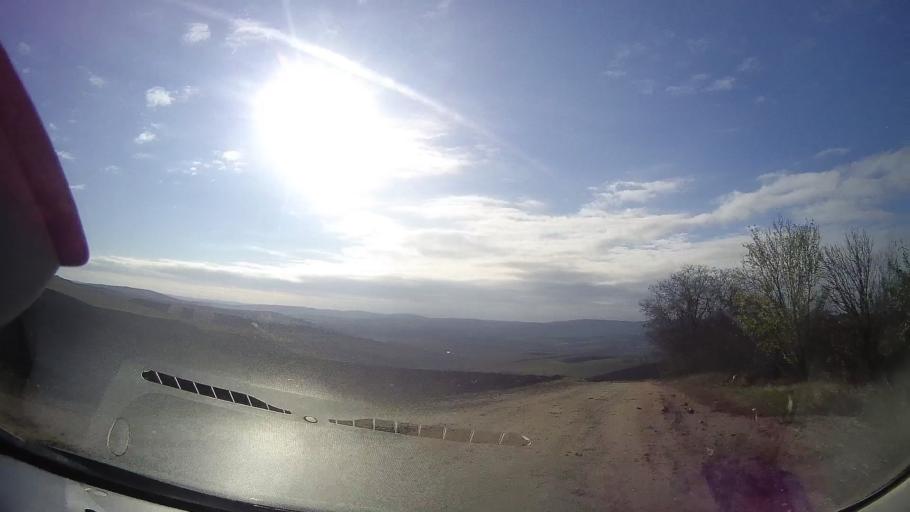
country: RO
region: Mures
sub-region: Comuna Papiu Ilarian
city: Papiu Ilarian
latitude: 46.5852
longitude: 24.2270
